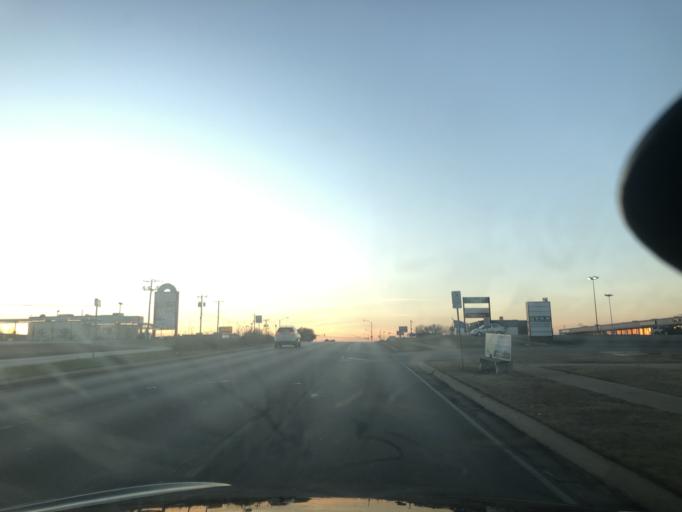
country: US
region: Texas
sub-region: Tarrant County
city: White Settlement
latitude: 32.7245
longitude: -97.4662
